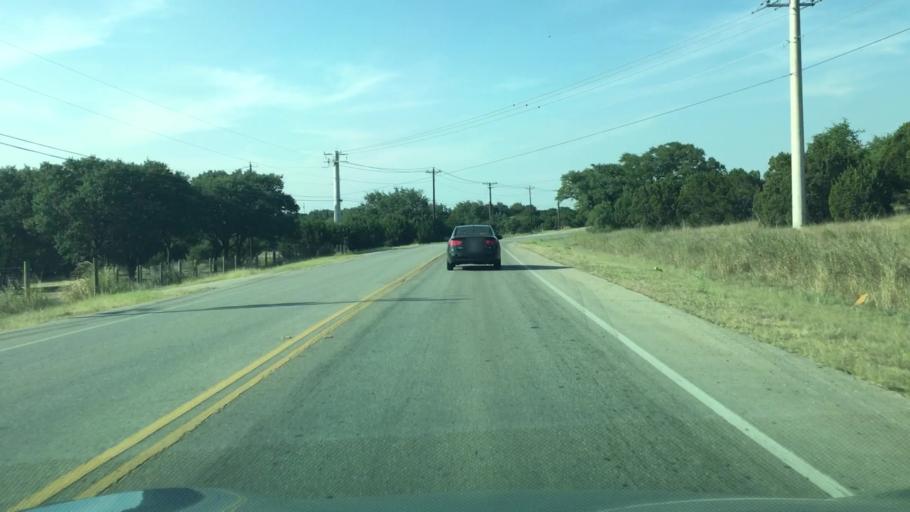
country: US
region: Texas
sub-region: Hays County
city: Dripping Springs
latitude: 30.1674
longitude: -98.0082
